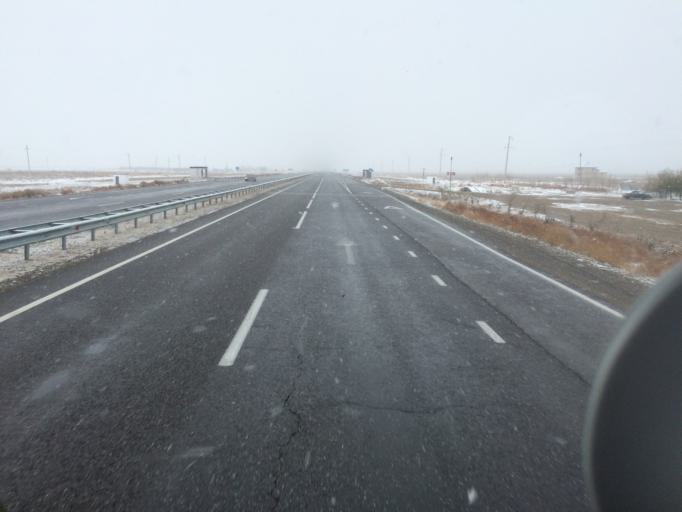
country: KZ
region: Ongtustik Qazaqstan
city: Turkestan
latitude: 43.4571
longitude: 67.9339
